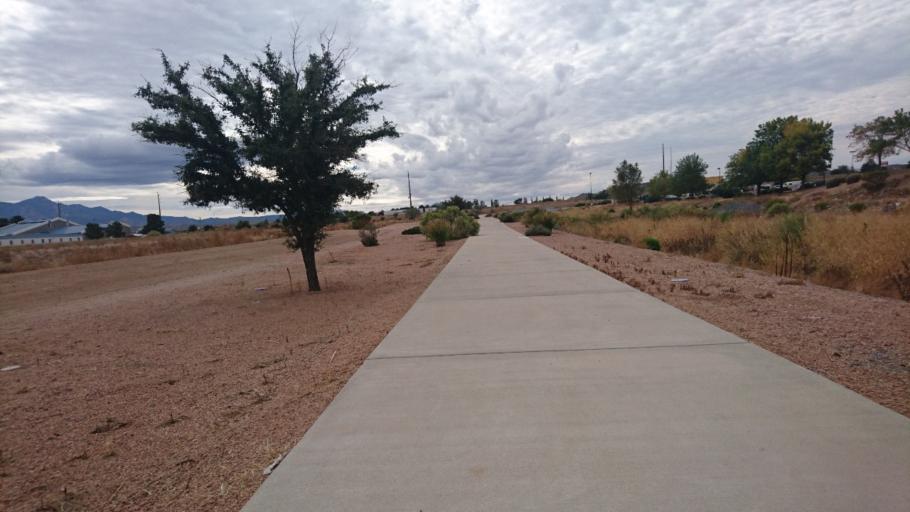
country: US
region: Arizona
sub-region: Mohave County
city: Kingman
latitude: 35.2209
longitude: -114.0315
